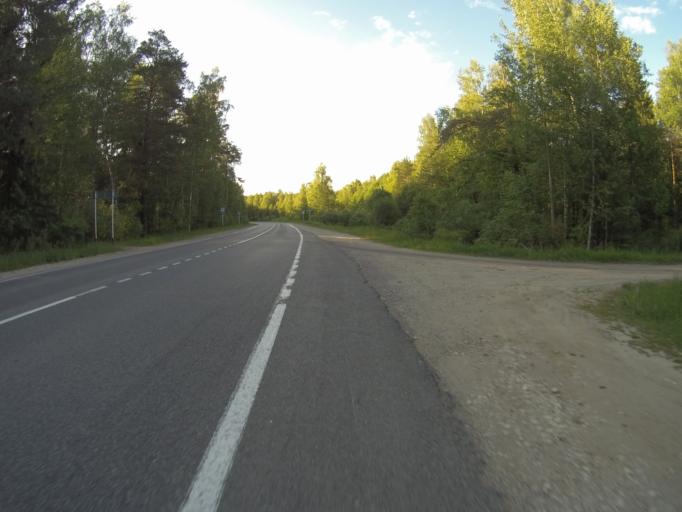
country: RU
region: Vladimir
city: Anopino
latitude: 55.8937
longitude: 40.6197
